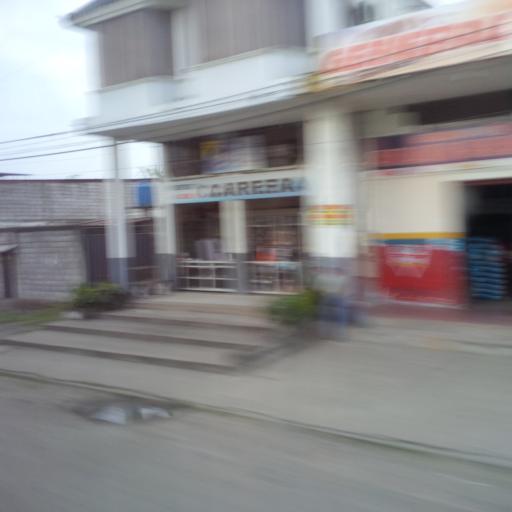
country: EC
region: Canar
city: La Troncal
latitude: -2.3364
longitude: -79.3941
